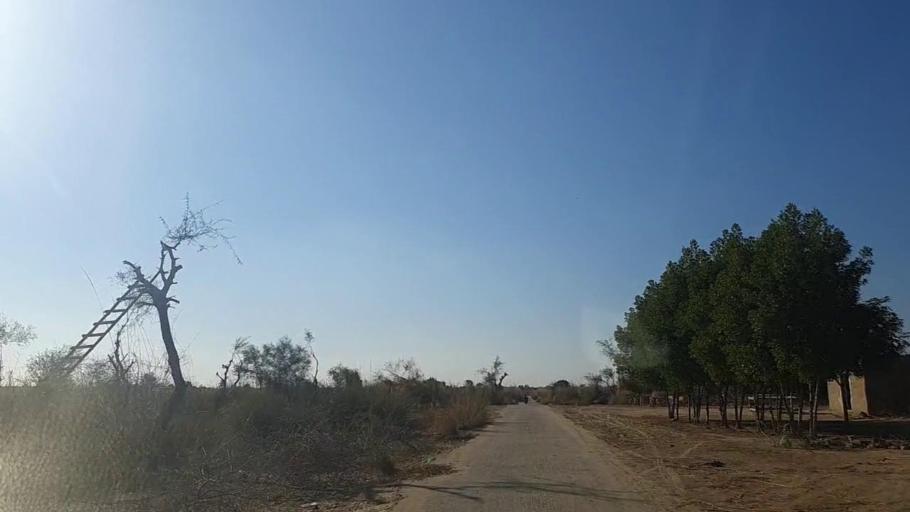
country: PK
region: Sindh
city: Sanghar
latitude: 26.2417
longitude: 68.8982
